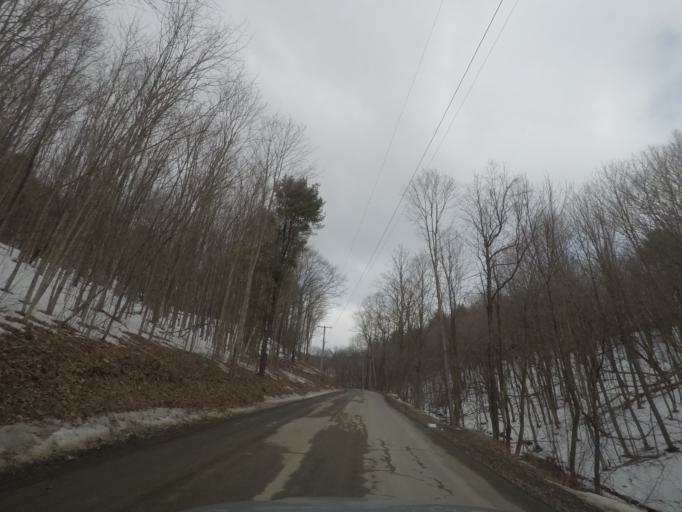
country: US
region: New York
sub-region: Saratoga County
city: Waterford
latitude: 42.7772
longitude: -73.6119
